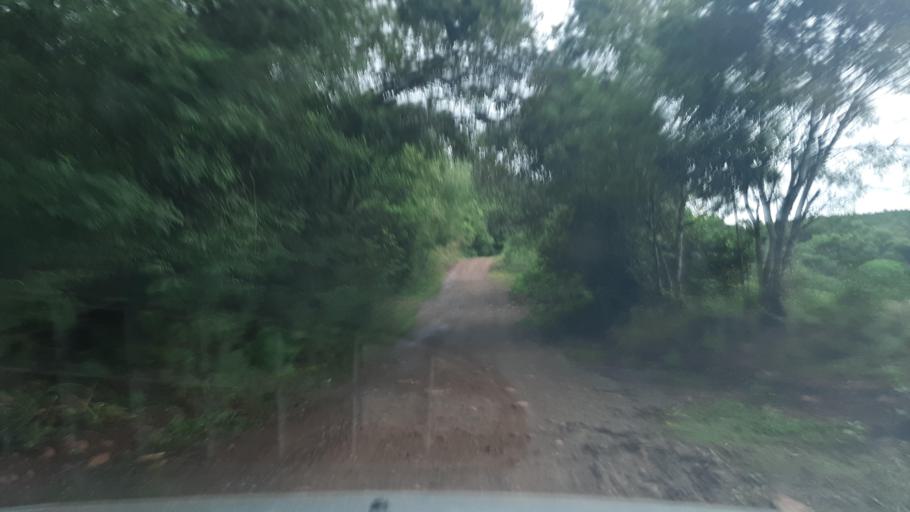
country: BR
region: Parana
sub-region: Ampere
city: Ampere
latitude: -26.0577
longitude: -53.5474
